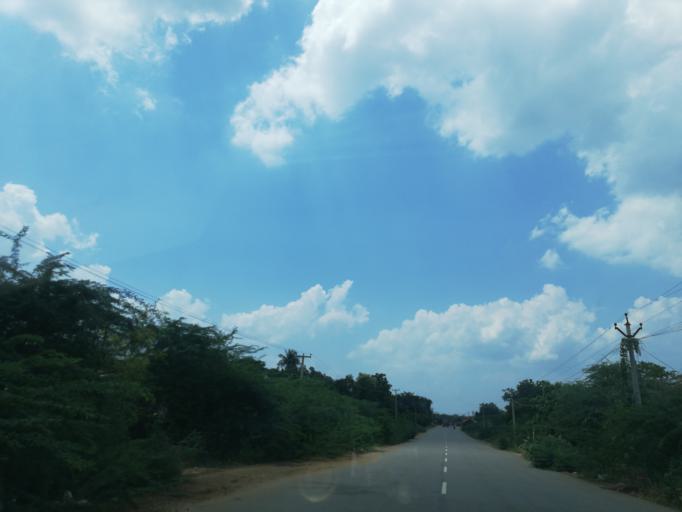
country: IN
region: Andhra Pradesh
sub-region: Guntur
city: Macherla
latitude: 16.5894
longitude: 79.3190
